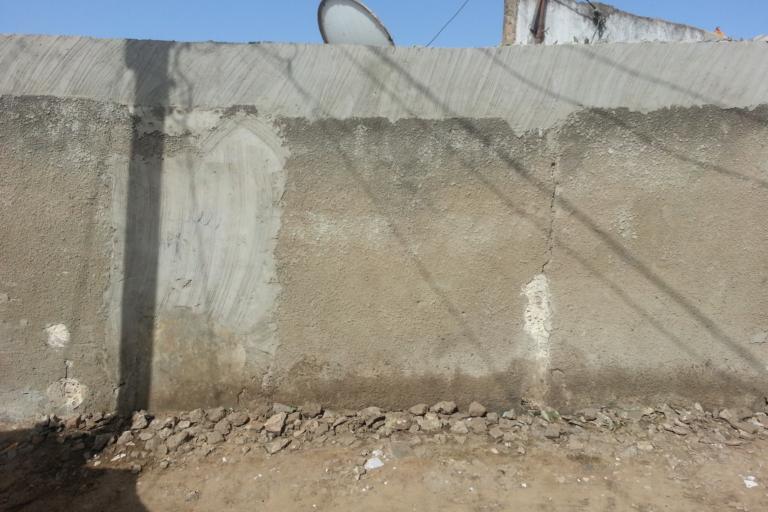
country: SN
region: Dakar
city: Pikine
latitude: 14.7729
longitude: -17.3815
